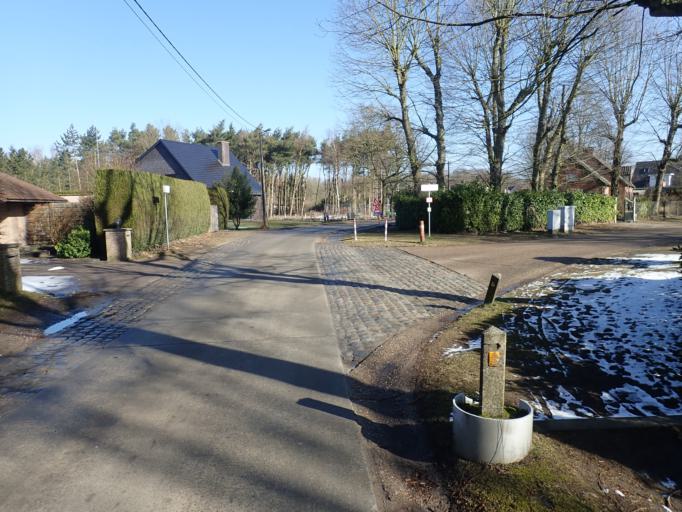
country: BE
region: Flanders
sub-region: Provincie Antwerpen
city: Lier
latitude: 51.1466
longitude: 4.6001
